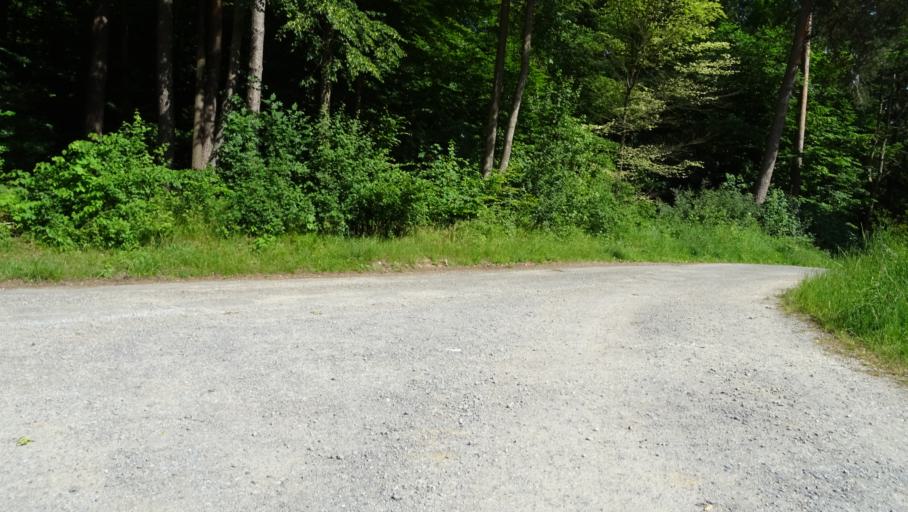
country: DE
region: Baden-Wuerttemberg
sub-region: Karlsruhe Region
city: Adelsheim
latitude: 49.4103
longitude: 9.3654
